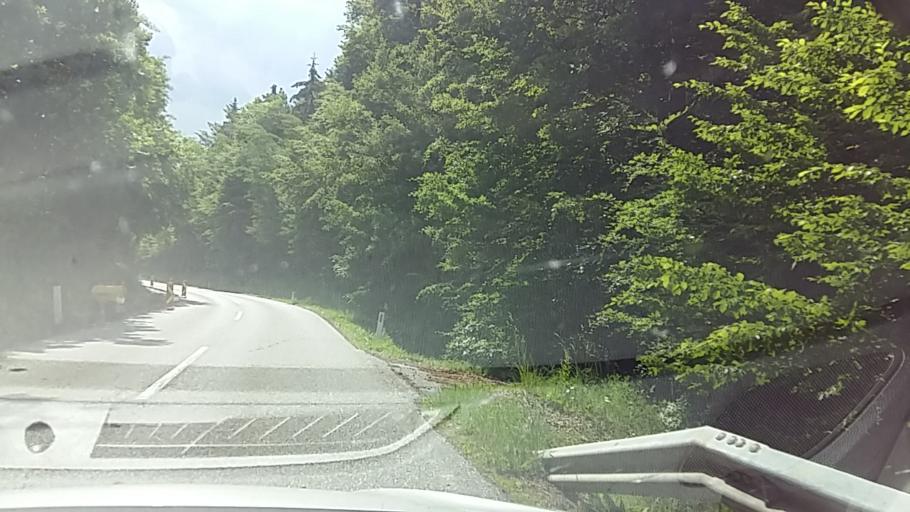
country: AT
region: Styria
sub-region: Politischer Bezirk Suedoststeiermark
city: Breitenfeld an der Rittschein
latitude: 47.0274
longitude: 15.9527
